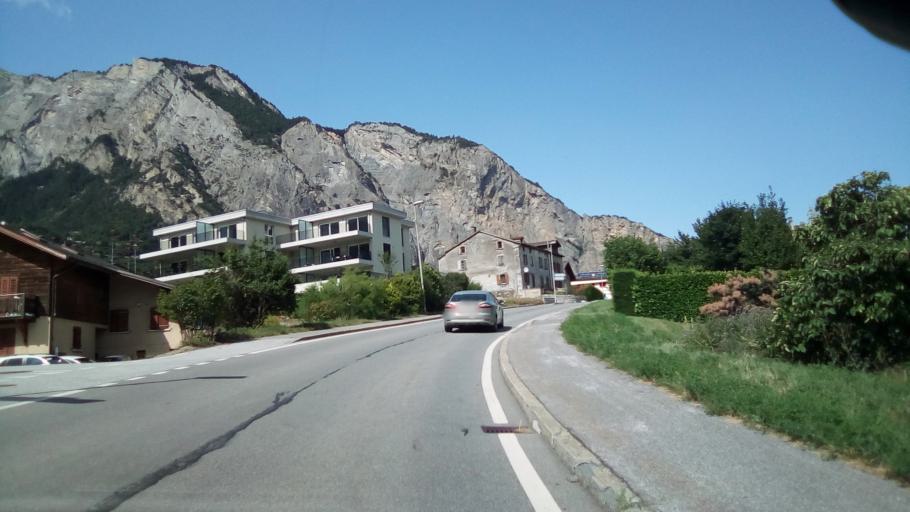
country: CH
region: Valais
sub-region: Conthey District
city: Chamoson
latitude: 46.1978
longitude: 7.2210
